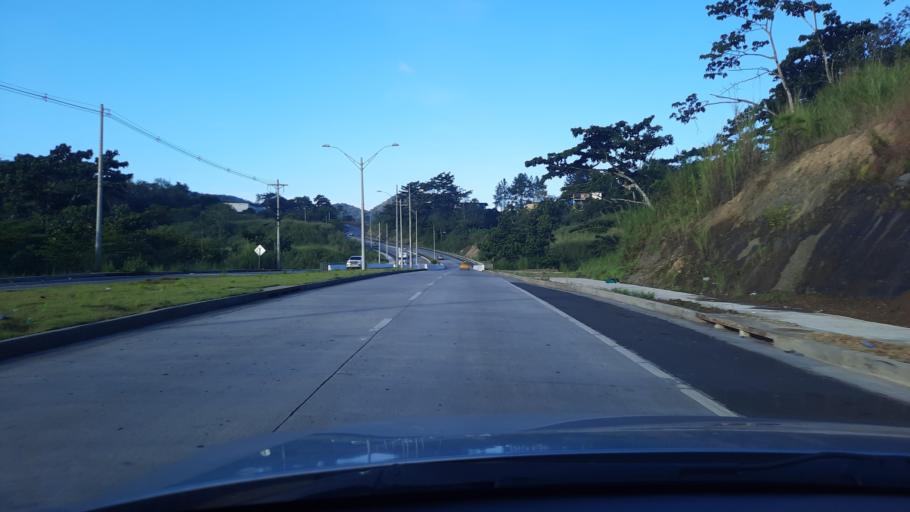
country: PA
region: Panama
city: Las Cumbres
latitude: 9.1044
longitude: -79.5288
